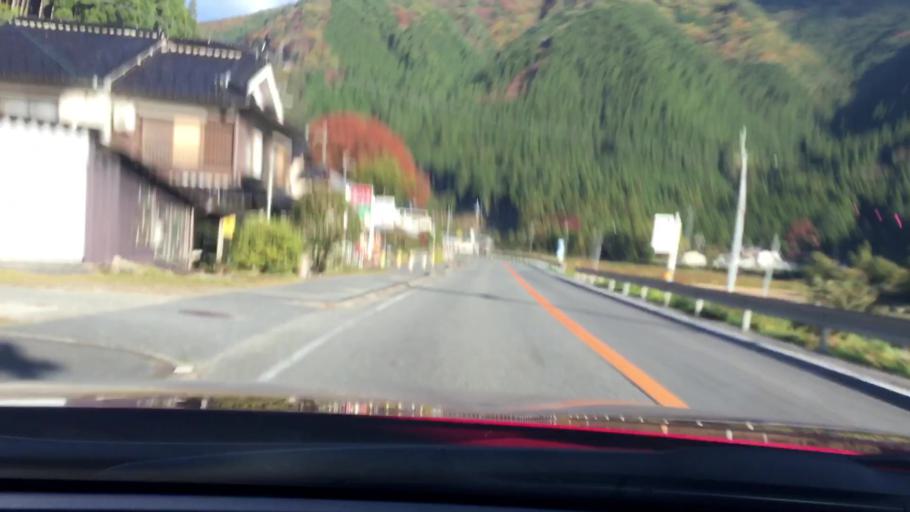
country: JP
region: Hyogo
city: Yamazakicho-nakabirose
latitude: 35.1369
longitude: 134.5565
